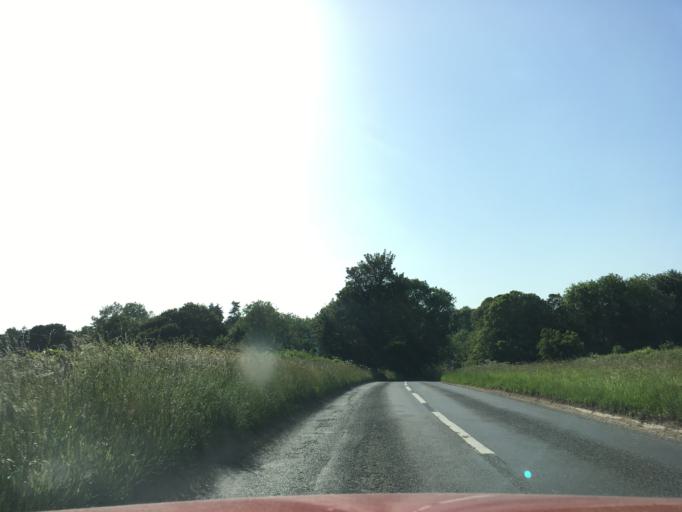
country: GB
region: England
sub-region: Oxfordshire
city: Deddington
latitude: 51.9259
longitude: -1.3415
